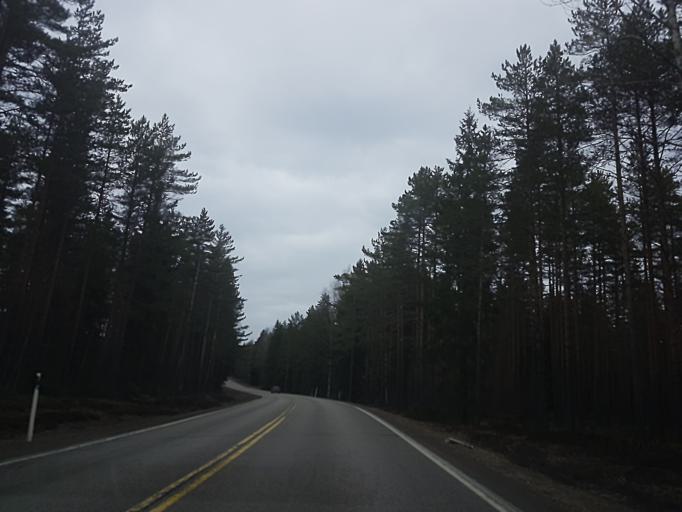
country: FI
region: Kymenlaakso
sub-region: Kotka-Hamina
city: Hamina
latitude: 60.7610
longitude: 27.3495
